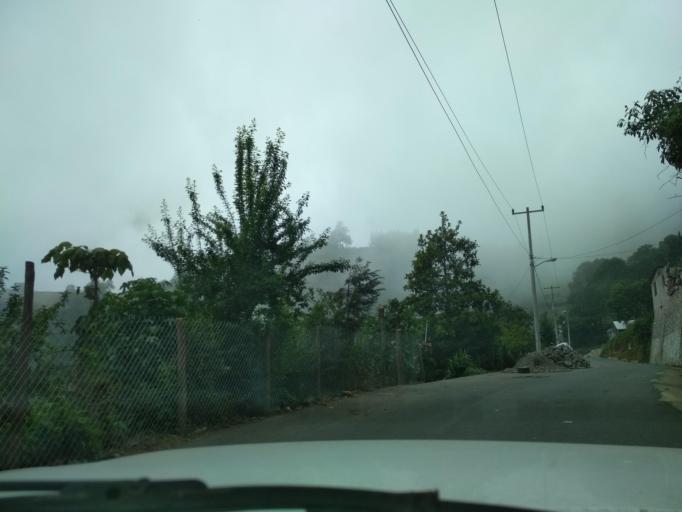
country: MX
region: Veracruz
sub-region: Mariano Escobedo
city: San Isidro el Berro
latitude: 18.9453
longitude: -97.1992
